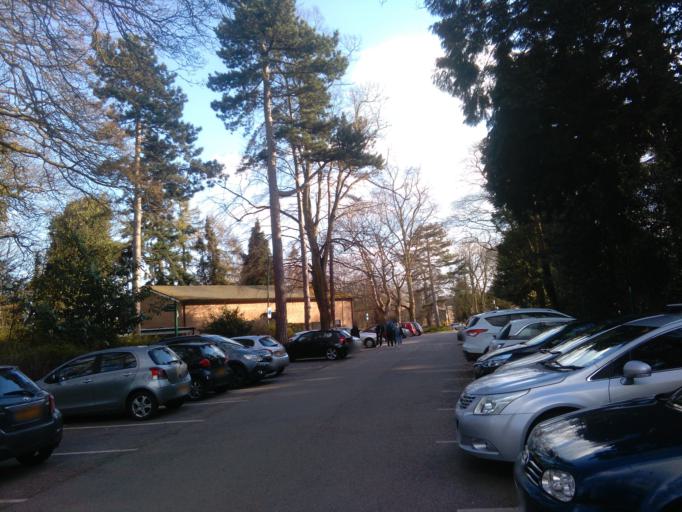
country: GB
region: England
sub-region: Nottingham
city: Nottingham
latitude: 52.9440
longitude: -1.1963
